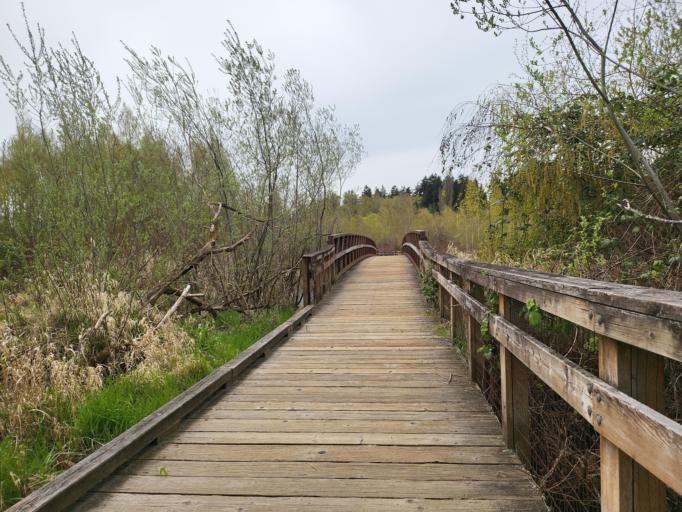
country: US
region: Washington
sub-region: King County
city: Newport
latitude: 47.5893
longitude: -122.1865
